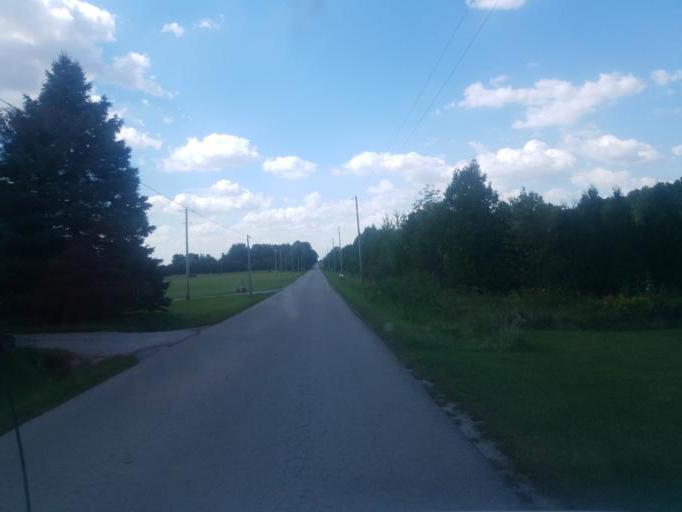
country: US
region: Ohio
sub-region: Logan County
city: Lakeview
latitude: 40.6517
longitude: -83.9464
